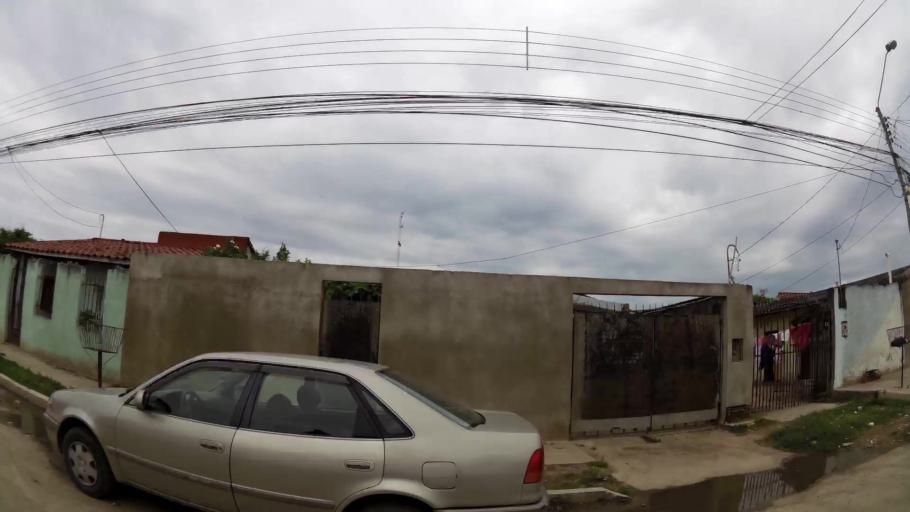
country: BO
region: Santa Cruz
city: Santa Cruz de la Sierra
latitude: -17.7456
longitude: -63.1857
